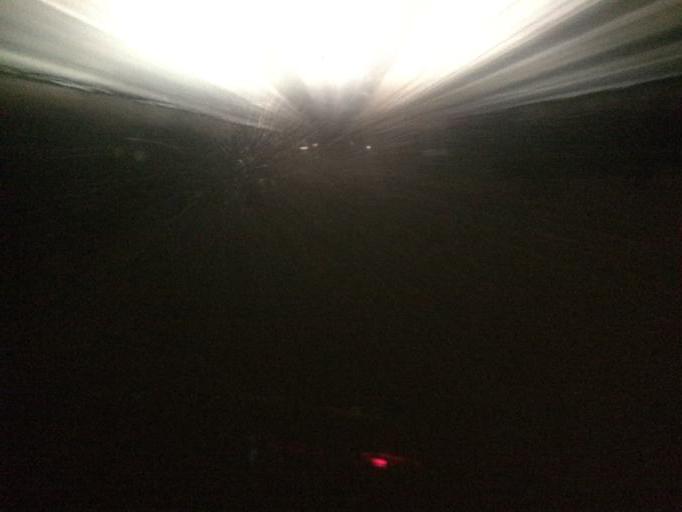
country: RU
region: Tula
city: Kosaya Gora
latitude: 54.1496
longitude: 37.4311
